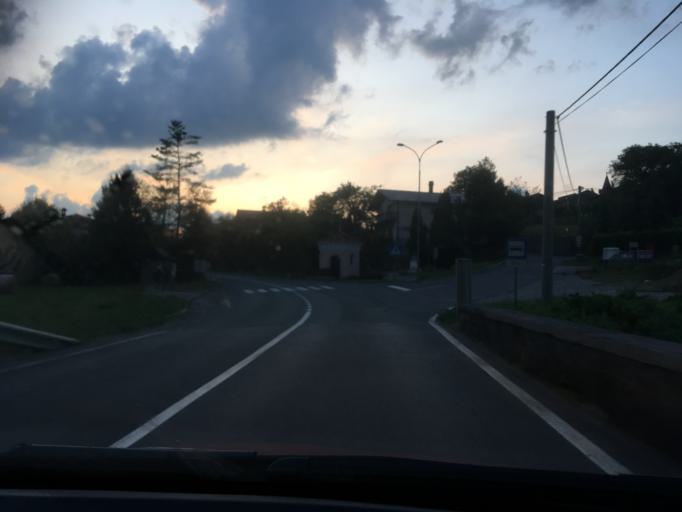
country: SI
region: Ilirska Bistrica
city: Ilirska Bistrica
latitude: 45.5826
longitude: 14.2177
